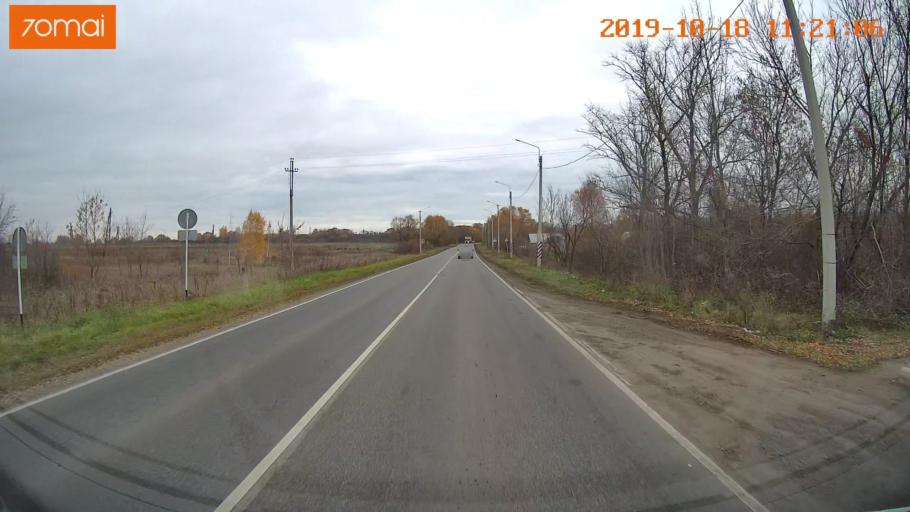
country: RU
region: Tula
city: Kimovsk
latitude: 54.0700
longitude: 38.5624
